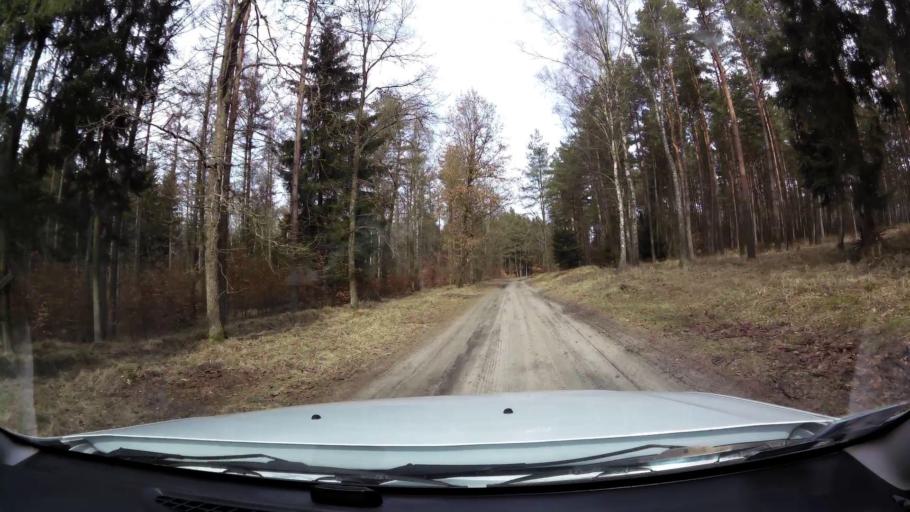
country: PL
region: West Pomeranian Voivodeship
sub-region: Powiat drawski
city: Drawsko Pomorskie
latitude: 53.4913
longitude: 15.7012
